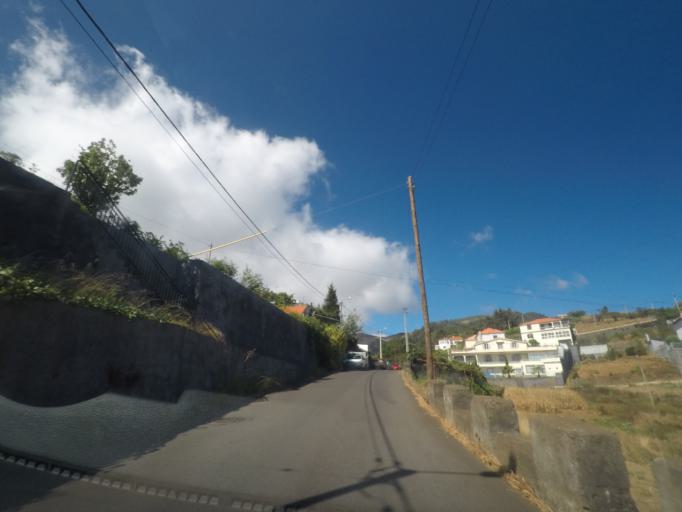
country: PT
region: Madeira
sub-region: Ribeira Brava
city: Campanario
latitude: 32.6974
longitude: -17.0265
